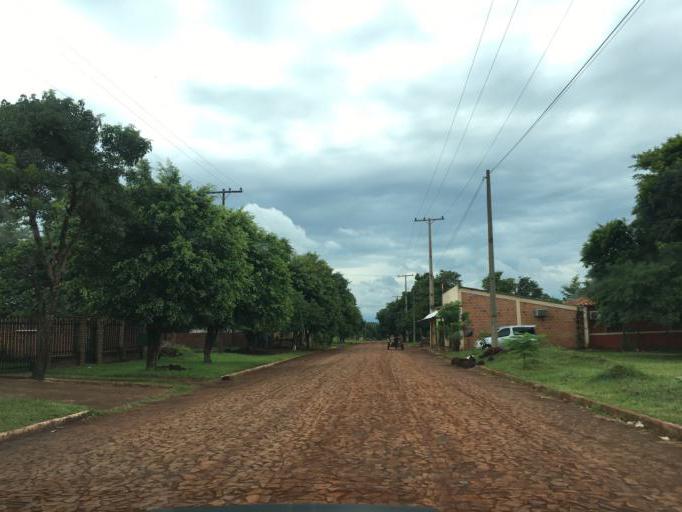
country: PY
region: Alto Parana
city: Ciudad del Este
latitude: -25.4186
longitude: -54.6431
